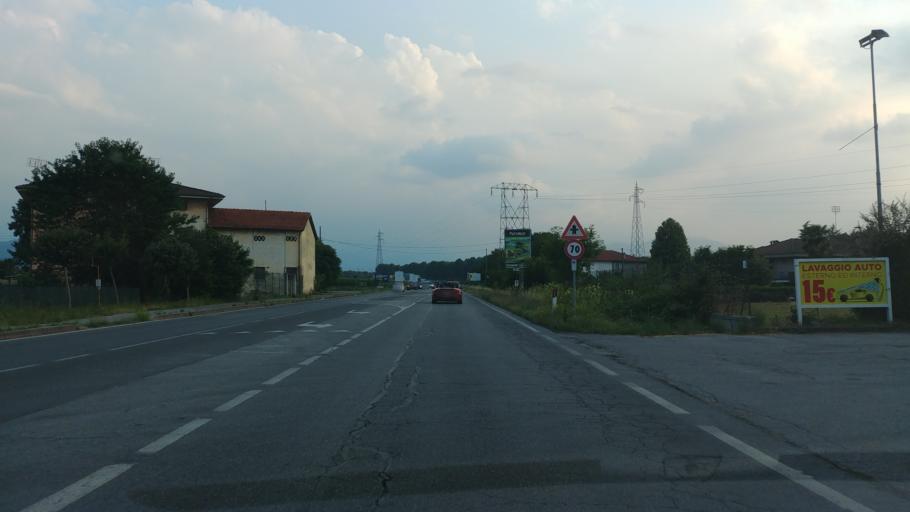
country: IT
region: Piedmont
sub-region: Provincia di Cuneo
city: Cuneo
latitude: 44.3730
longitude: 7.5227
